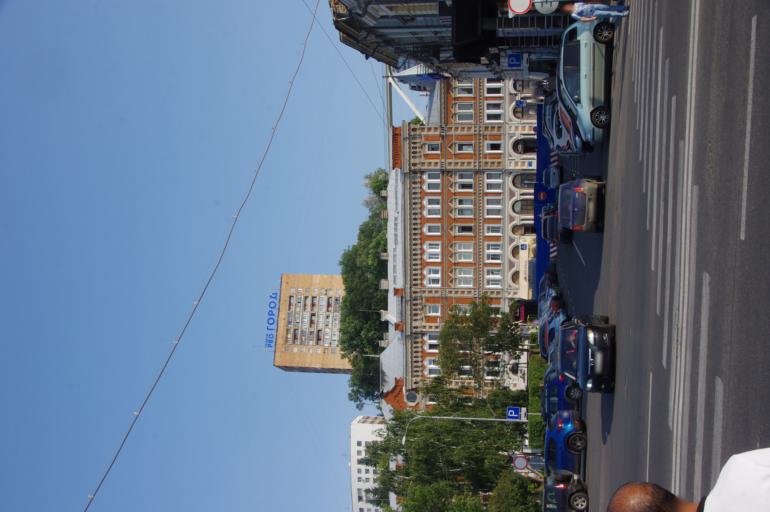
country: RU
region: Nizjnij Novgorod
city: Nizhniy Novgorod
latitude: 56.3292
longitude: 43.9869
